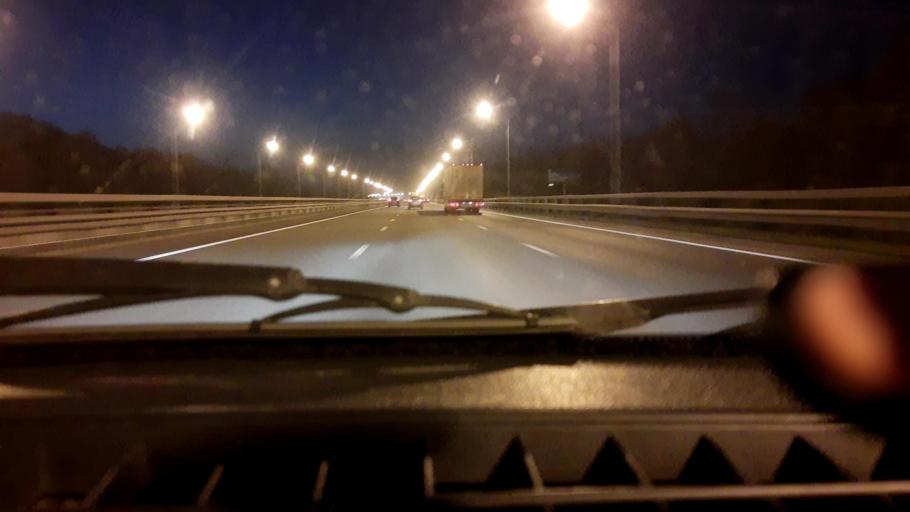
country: RU
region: Bashkortostan
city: Ufa
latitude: 54.6525
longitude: 55.9022
